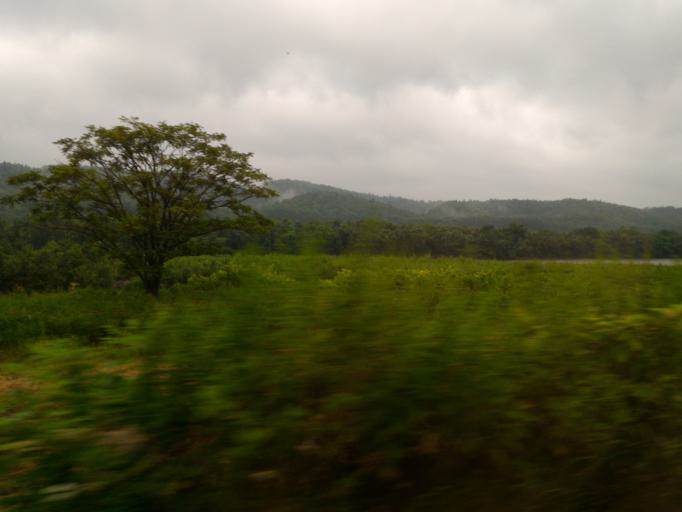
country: JP
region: Hokkaido
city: Nayoro
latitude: 44.7555
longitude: 142.0477
